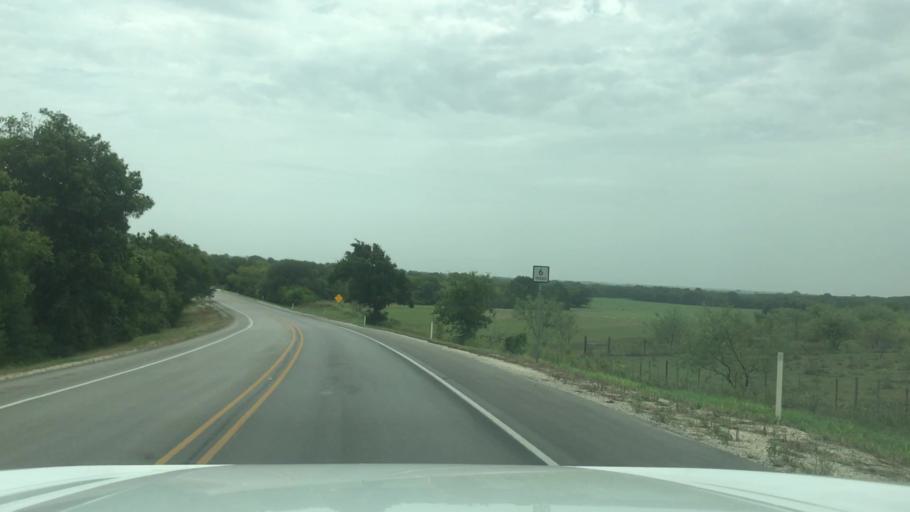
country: US
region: Texas
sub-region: Erath County
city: Dublin
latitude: 32.0752
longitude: -98.2337
